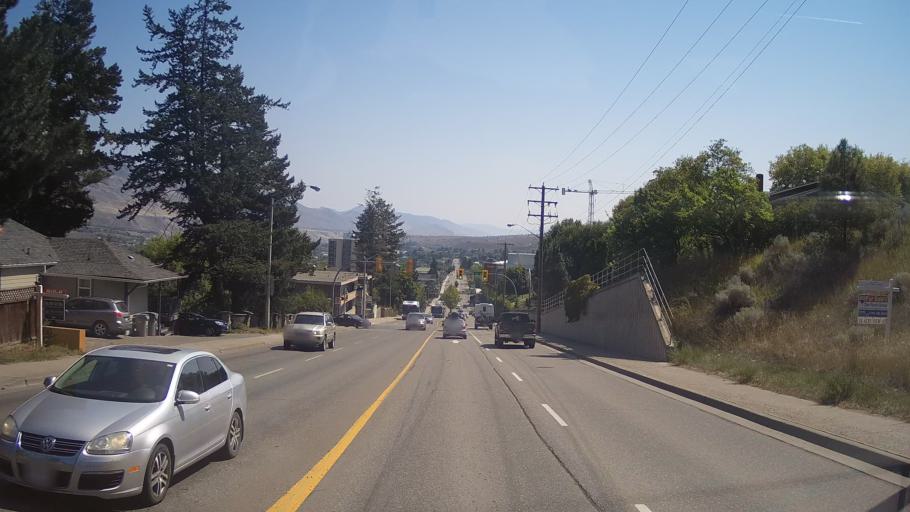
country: CA
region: British Columbia
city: Kamloops
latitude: 50.6715
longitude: -120.3404
